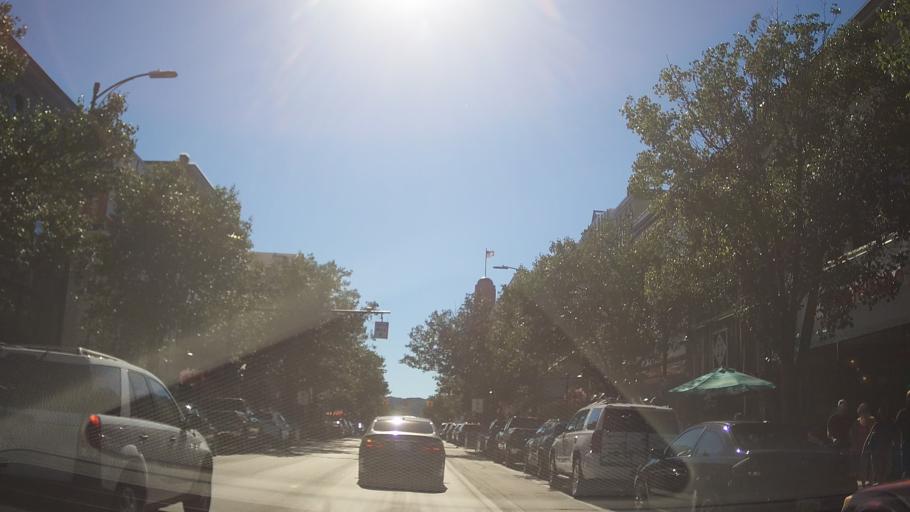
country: US
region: Michigan
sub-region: Grand Traverse County
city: Traverse City
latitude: 44.7641
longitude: -85.6222
